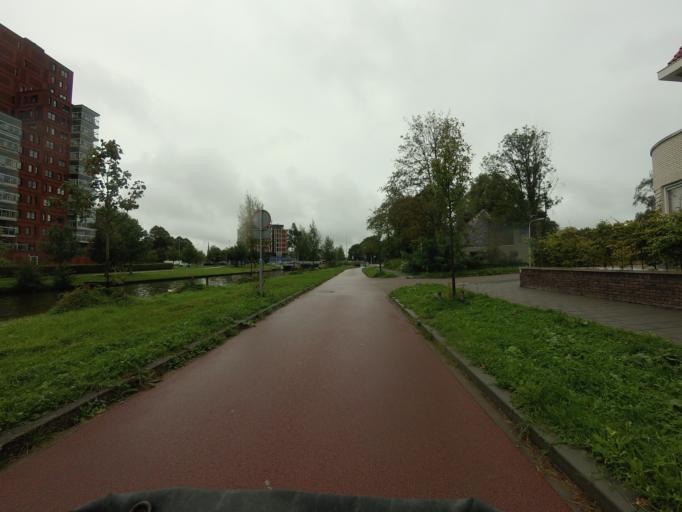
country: NL
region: Friesland
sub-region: Gemeente Leeuwarden
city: Bilgaard
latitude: 53.2144
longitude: 5.8040
